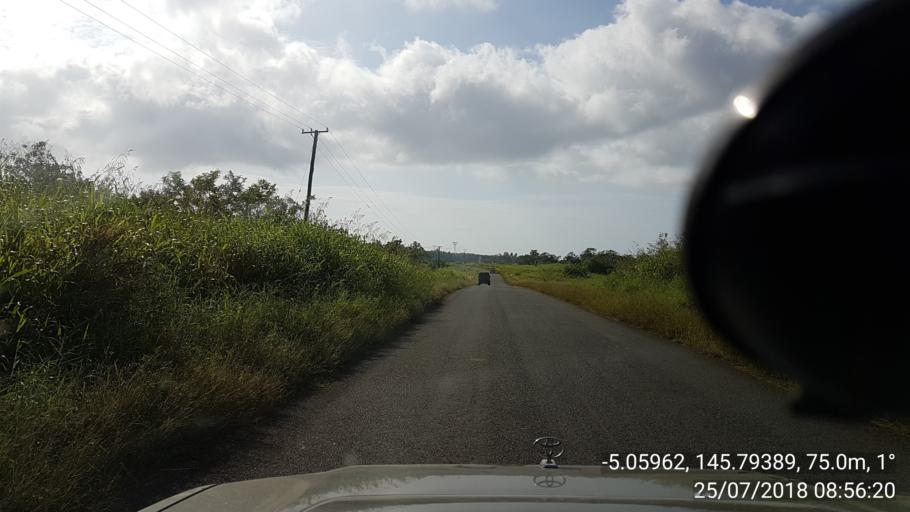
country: PG
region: Madang
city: Madang
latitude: -5.0597
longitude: 145.7936
